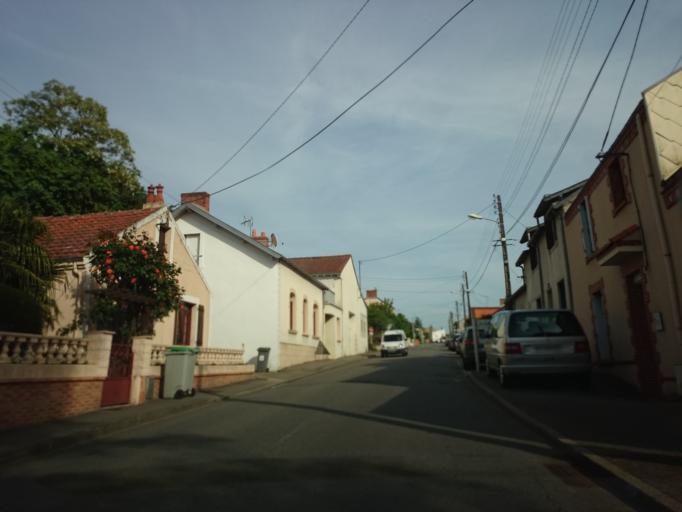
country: FR
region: Pays de la Loire
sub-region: Departement de la Loire-Atlantique
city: La Montagne
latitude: 47.1917
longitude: -1.6957
